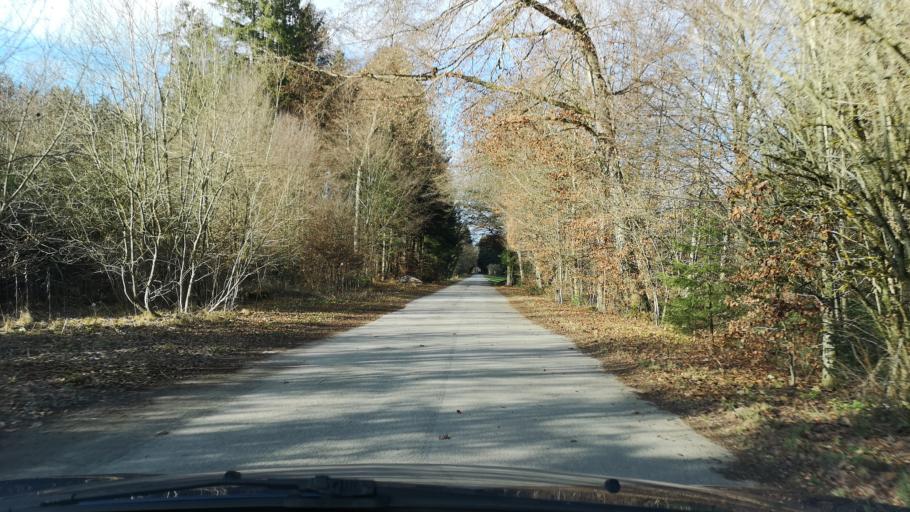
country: DE
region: Bavaria
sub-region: Upper Bavaria
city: Ebersberg
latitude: 48.0974
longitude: 11.9518
